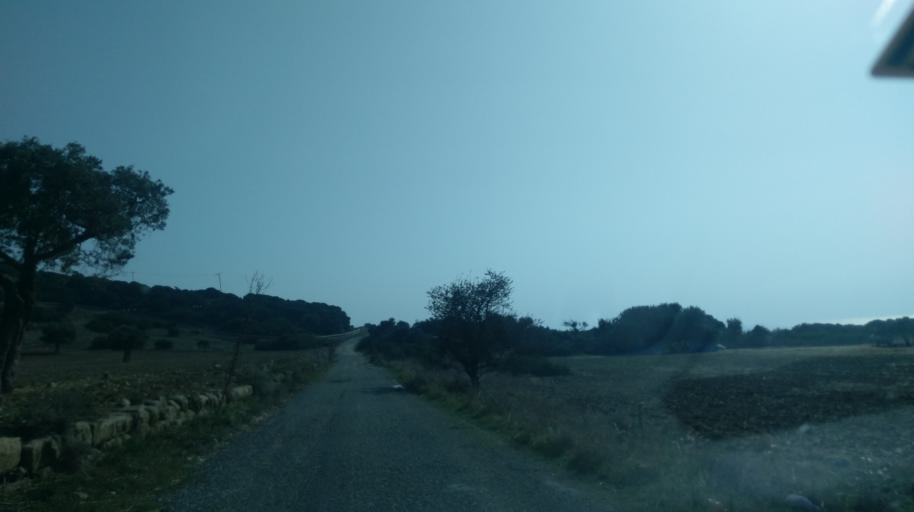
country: CY
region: Ammochostos
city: Rizokarpaso
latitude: 35.6476
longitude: 34.5527
